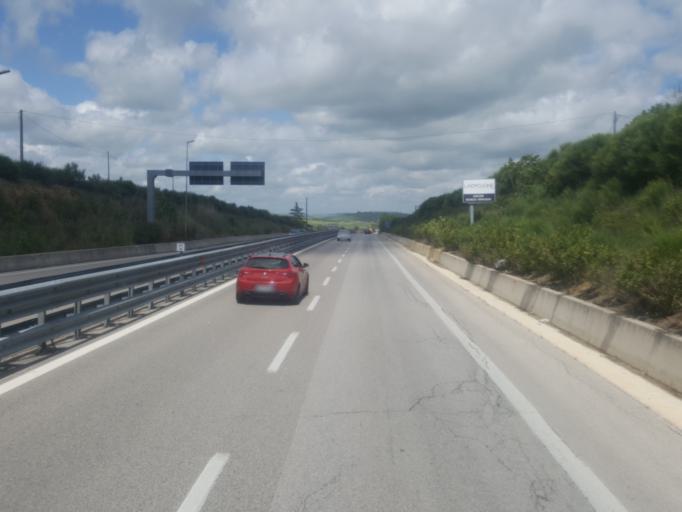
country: IT
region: Basilicate
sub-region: Provincia di Matera
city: Matera
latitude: 40.7026
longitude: 16.5859
